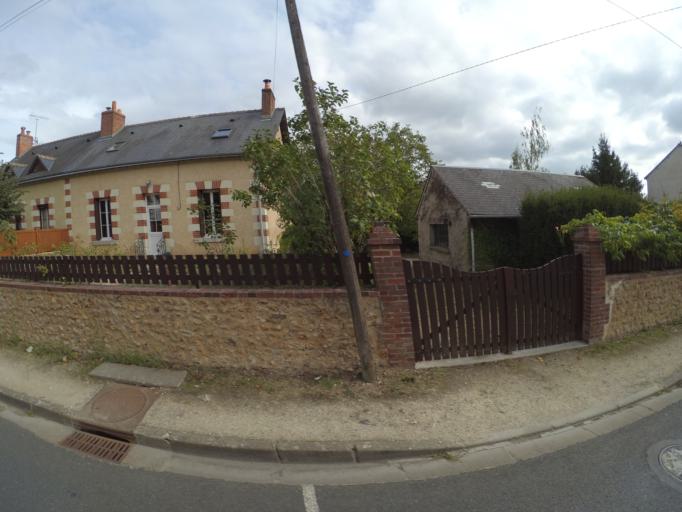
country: FR
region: Centre
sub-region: Departement d'Indre-et-Loire
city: Reugny
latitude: 47.4795
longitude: 0.8830
